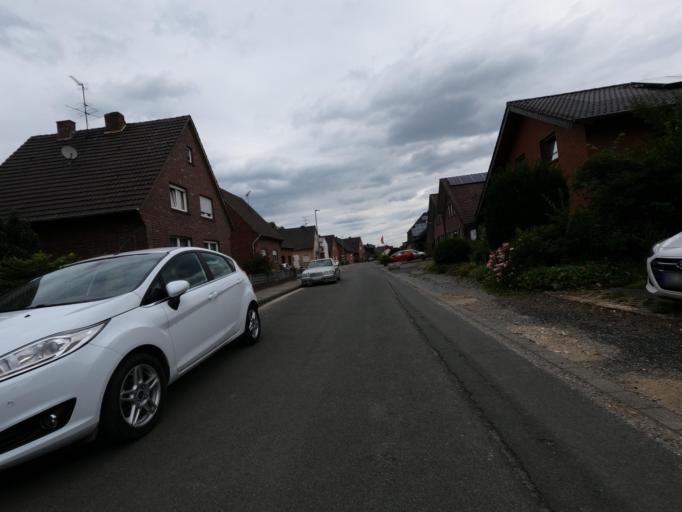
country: DE
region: North Rhine-Westphalia
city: Geilenkirchen
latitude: 51.0011
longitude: 6.1764
